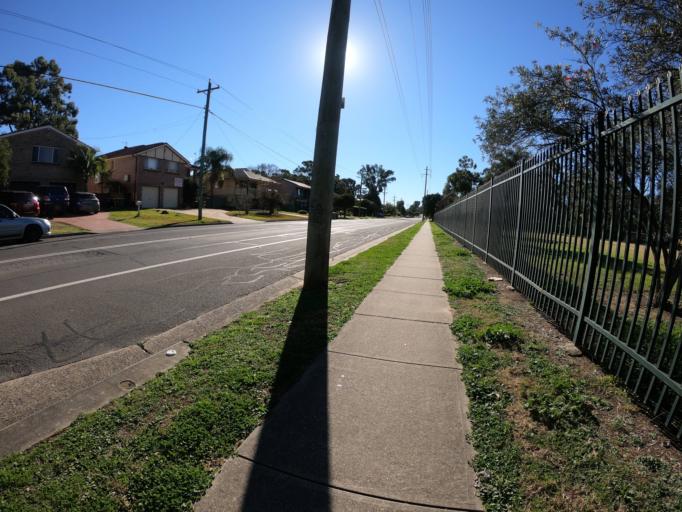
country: AU
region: New South Wales
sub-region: Hawkesbury
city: South Windsor
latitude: -33.6309
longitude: 150.7961
